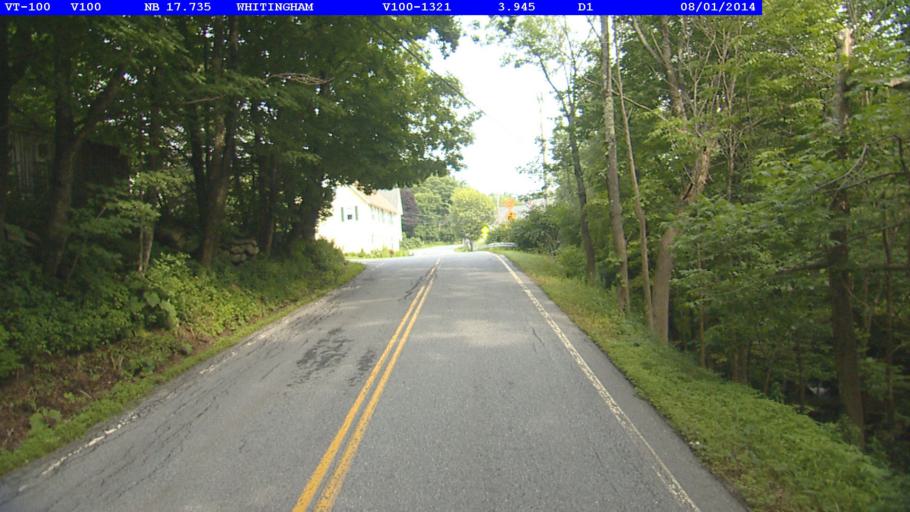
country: US
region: Massachusetts
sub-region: Franklin County
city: Charlemont
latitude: 42.7897
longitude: -72.8860
